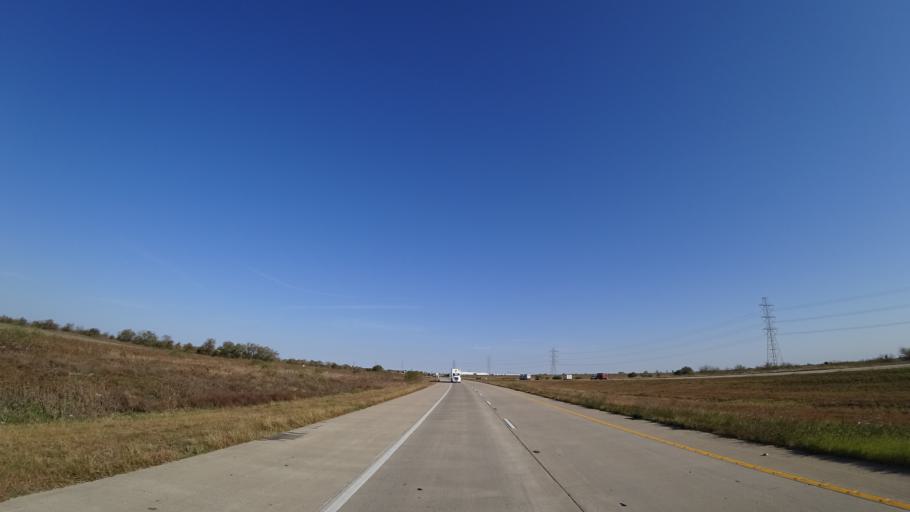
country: US
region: Texas
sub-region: Travis County
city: Manor
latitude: 30.3829
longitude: -97.5800
